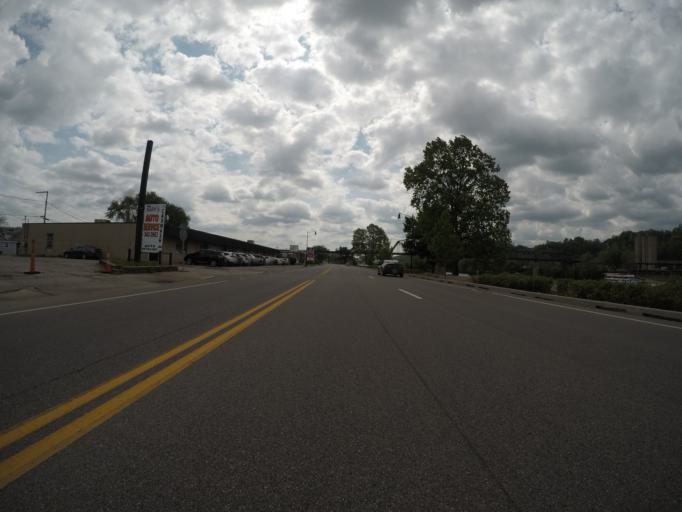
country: US
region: West Virginia
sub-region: Kanawha County
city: Charleston
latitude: 38.3651
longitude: -81.6641
